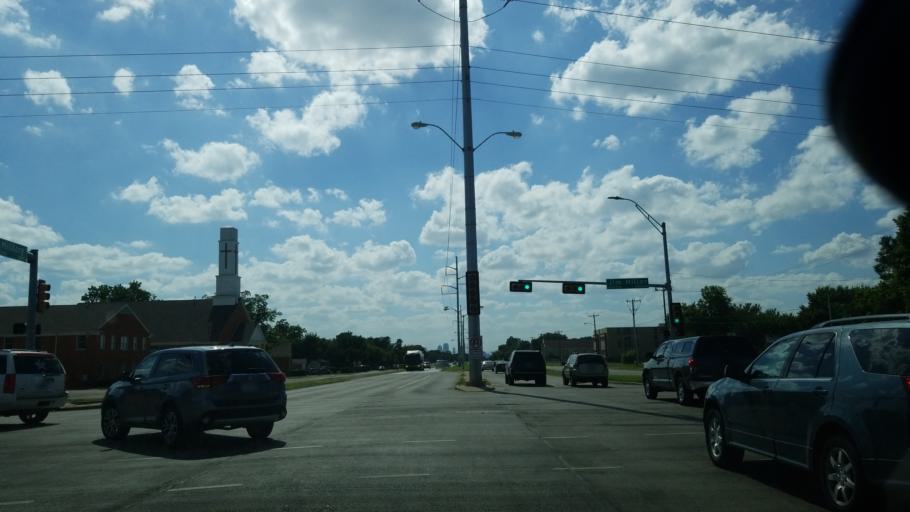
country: US
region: Texas
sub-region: Dallas County
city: Balch Springs
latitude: 32.7727
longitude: -96.6999
